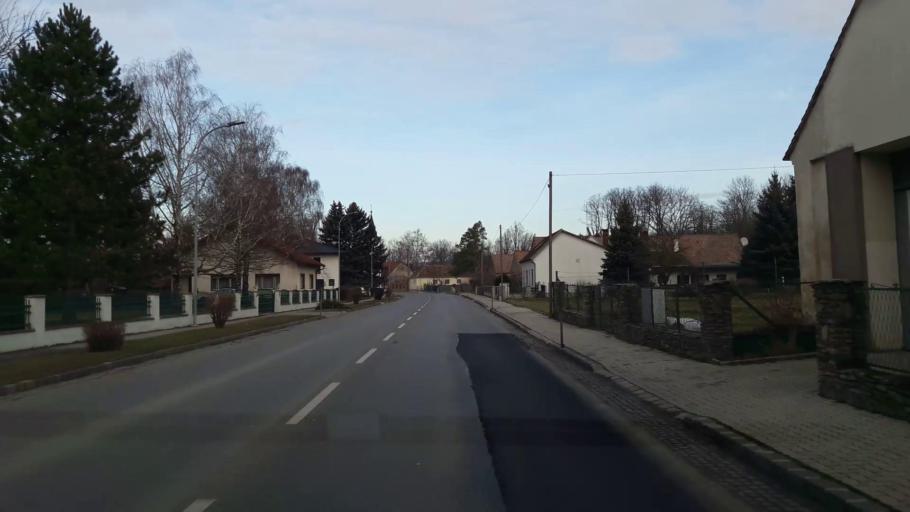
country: AT
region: Lower Austria
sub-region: Politischer Bezirk Mistelbach
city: Staatz
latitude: 48.6606
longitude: 16.4959
